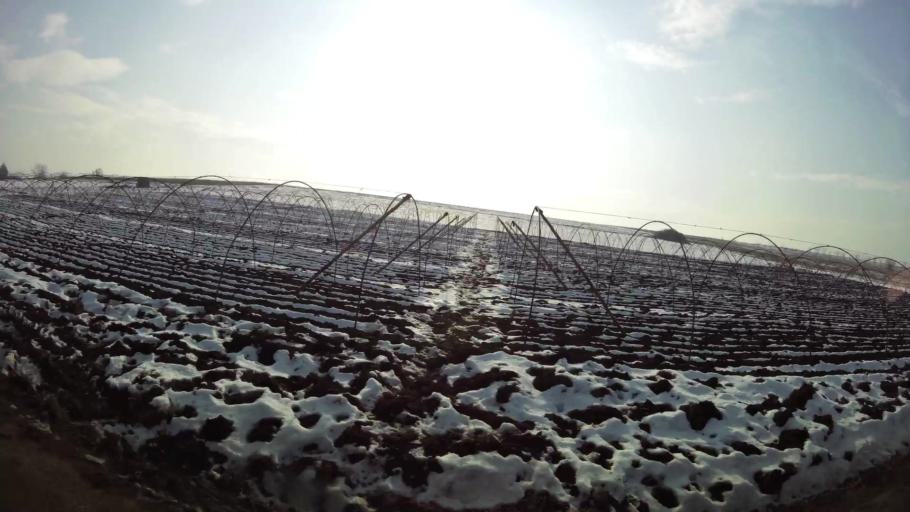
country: MK
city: Creshevo
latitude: 42.0141
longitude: 21.4927
